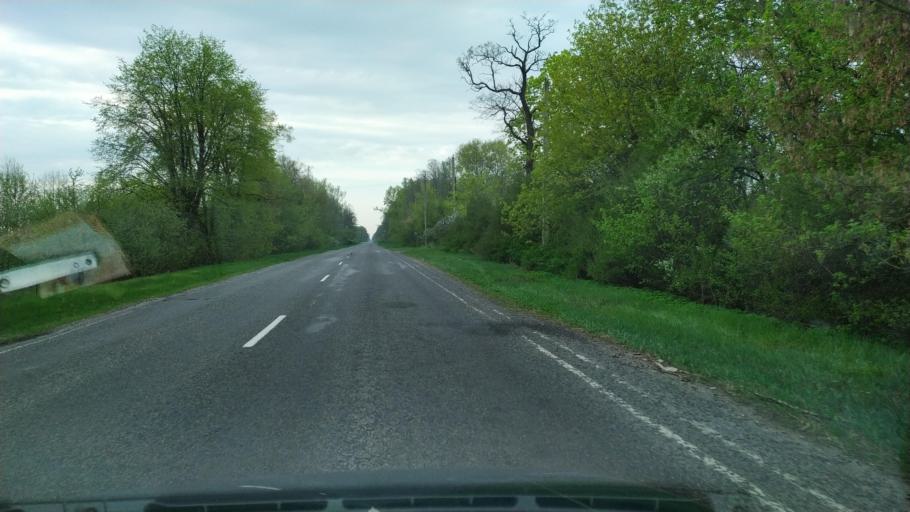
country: BY
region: Brest
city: Zhabinka
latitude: 52.2930
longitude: 23.9395
